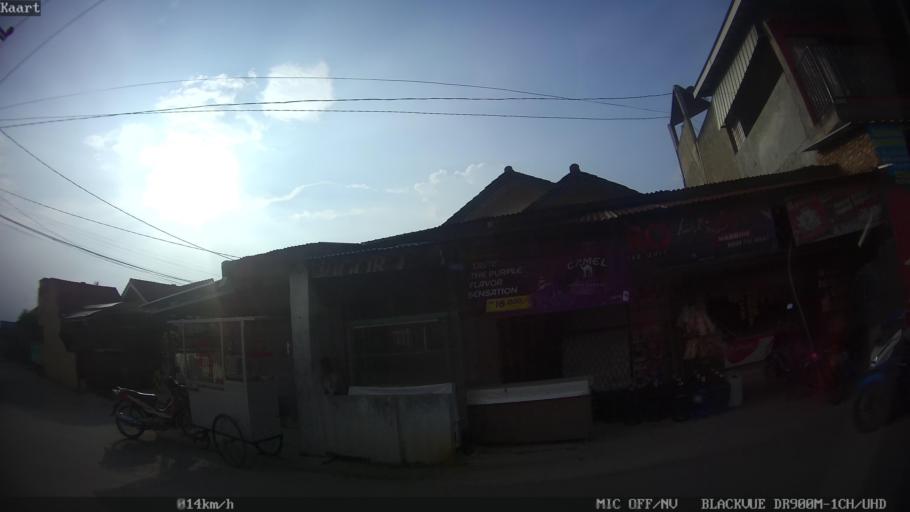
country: ID
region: Lampung
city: Kedaton
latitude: -5.4018
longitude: 105.3079
